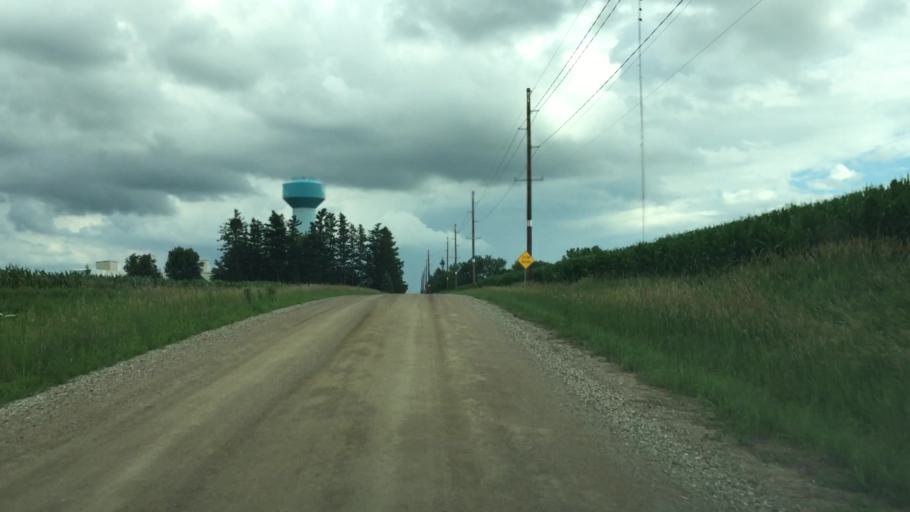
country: US
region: Iowa
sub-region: Jasper County
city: Newton
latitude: 41.7383
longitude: -93.0196
